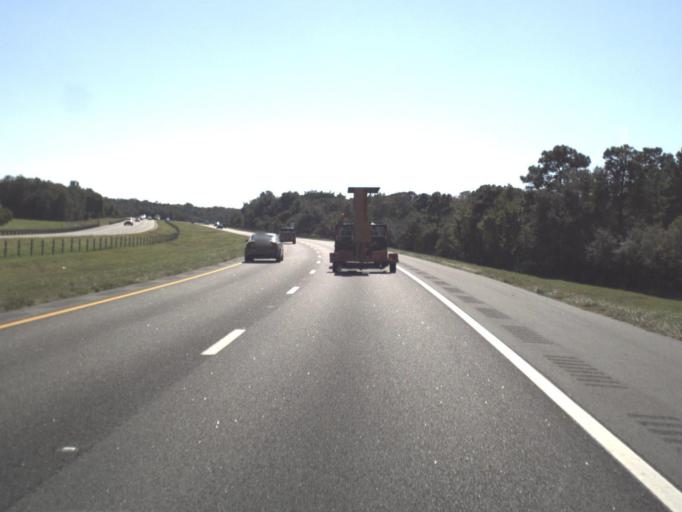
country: US
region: Florida
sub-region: Pasco County
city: Shady Hills
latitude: 28.3210
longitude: -82.5534
